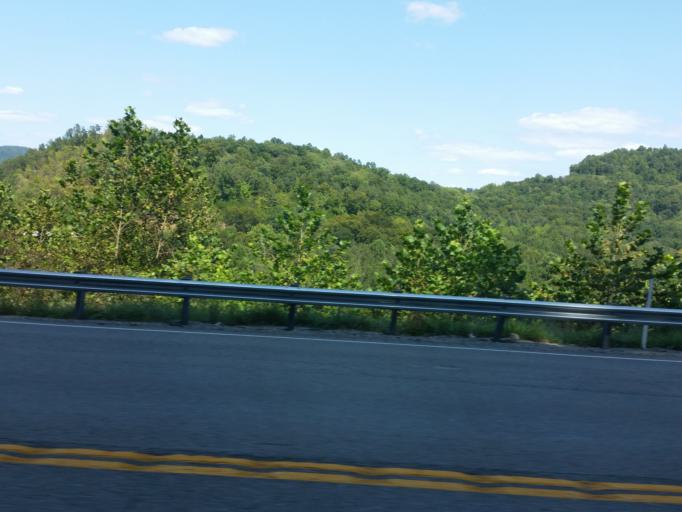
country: US
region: Kentucky
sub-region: Bell County
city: Pineville
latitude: 36.7417
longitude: -83.6109
